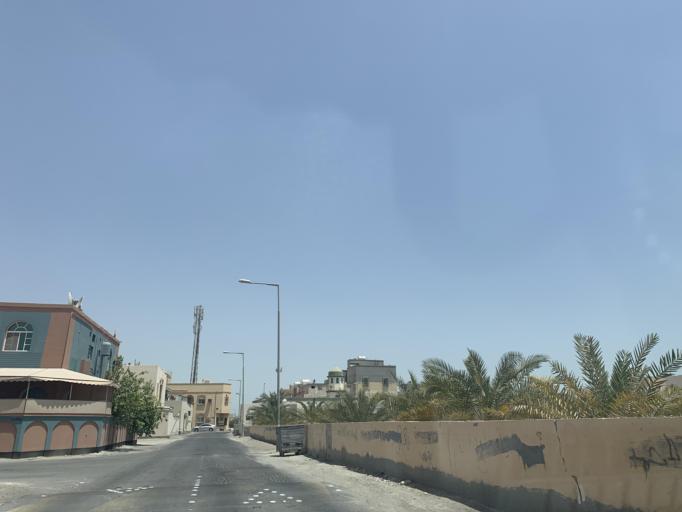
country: BH
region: Northern
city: Sitrah
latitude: 26.1575
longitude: 50.6216
